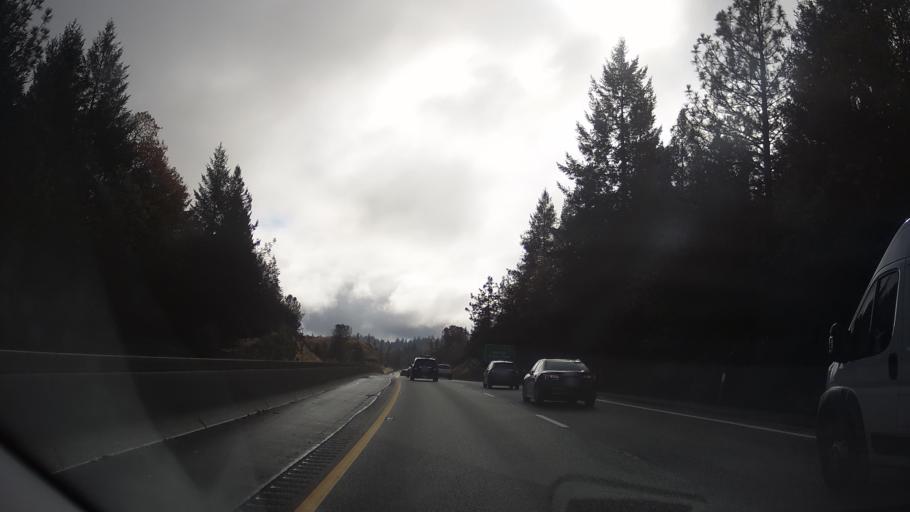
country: US
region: California
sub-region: Placer County
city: Colfax
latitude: 39.0614
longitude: -120.9682
